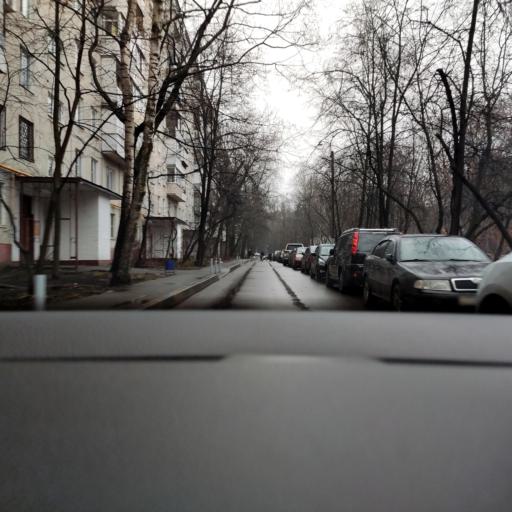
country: RU
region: Moscow
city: Ivanovskoye
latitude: 55.7642
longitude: 37.8255
